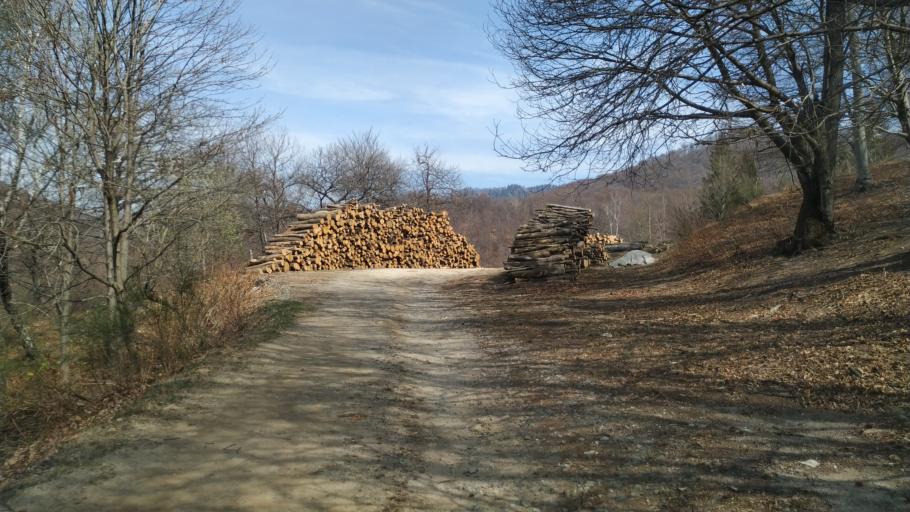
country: IT
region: Piedmont
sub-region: Provincia di Vercelli
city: Civiasco
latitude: 45.8053
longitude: 8.3137
